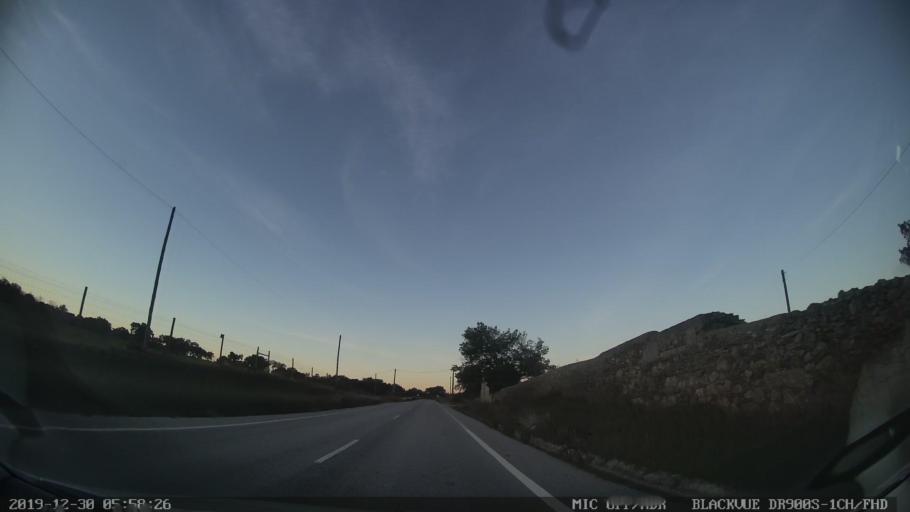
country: PT
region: Castelo Branco
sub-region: Idanha-A-Nova
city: Idanha-a-Nova
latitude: 40.0346
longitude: -7.2419
